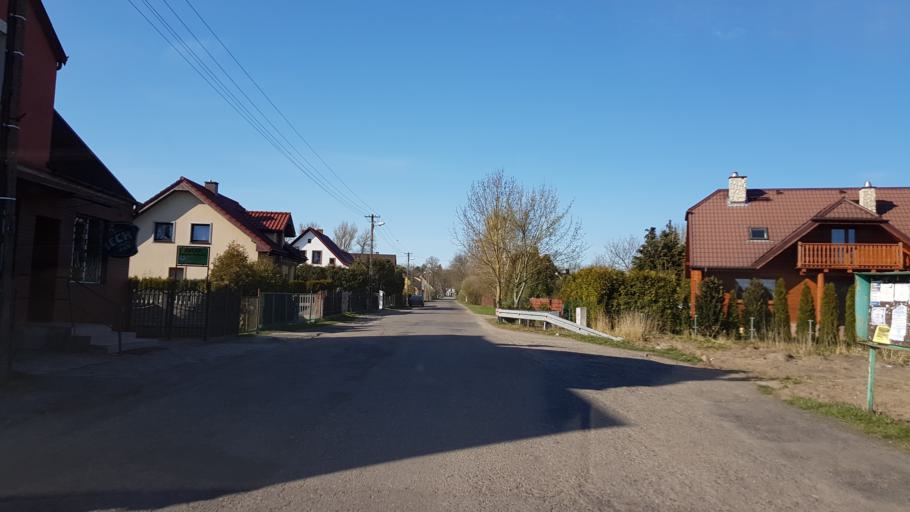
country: PL
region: West Pomeranian Voivodeship
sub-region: Powiat stargardzki
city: Stargard Szczecinski
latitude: 53.4015
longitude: 15.0294
